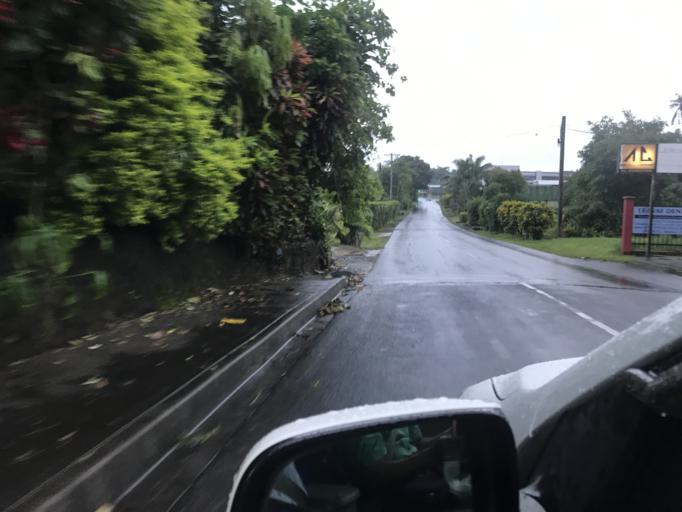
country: WS
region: Tuamasaga
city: Apia
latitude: -13.8365
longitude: -171.7633
